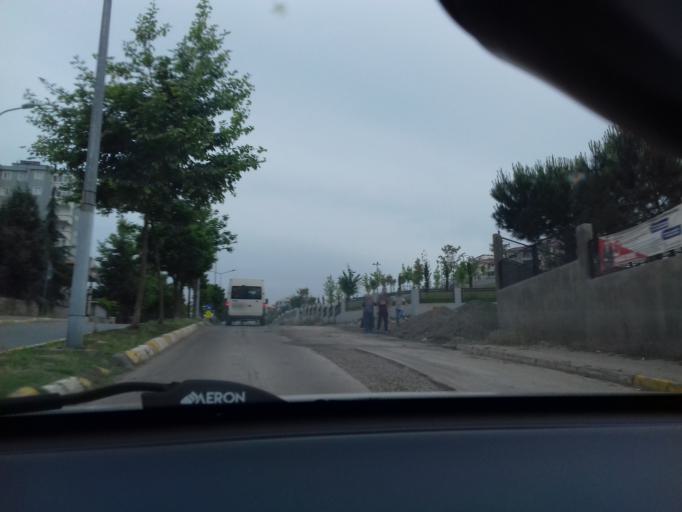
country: TR
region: Istanbul
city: Sultanbeyli
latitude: 40.9322
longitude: 29.3030
